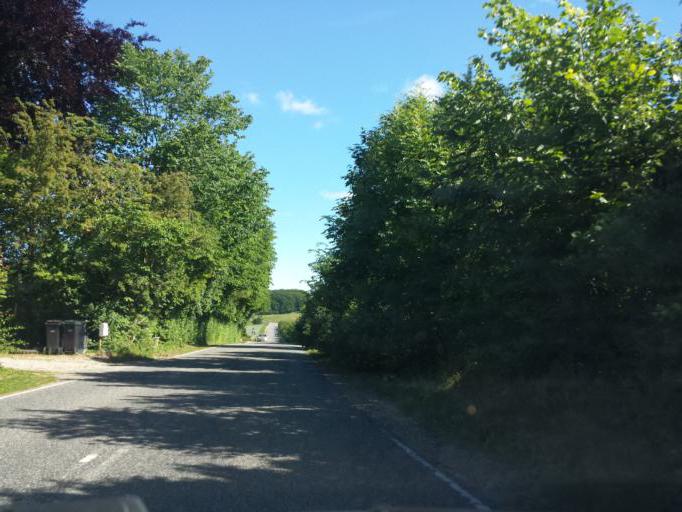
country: DK
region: Capital Region
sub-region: Egedal Kommune
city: Ganlose
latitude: 55.7979
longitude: 12.2639
